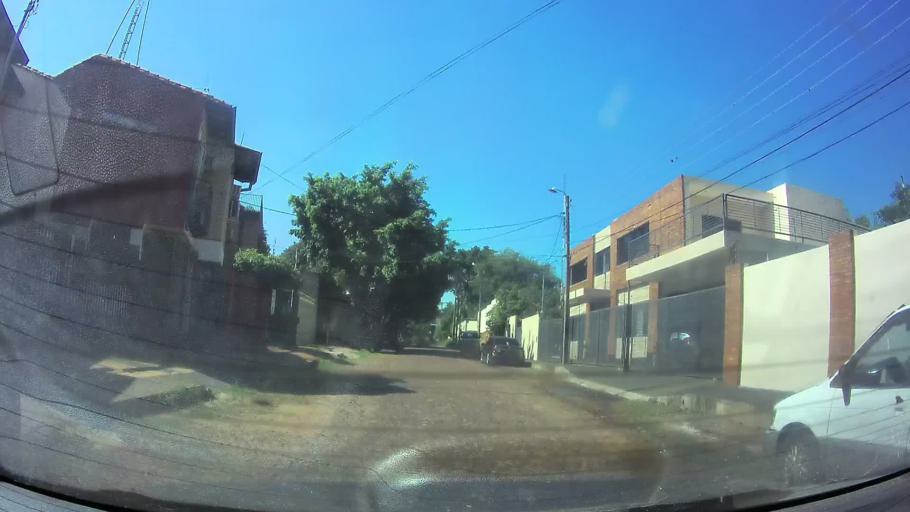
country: PY
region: Central
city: Fernando de la Mora
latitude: -25.3178
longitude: -57.5207
